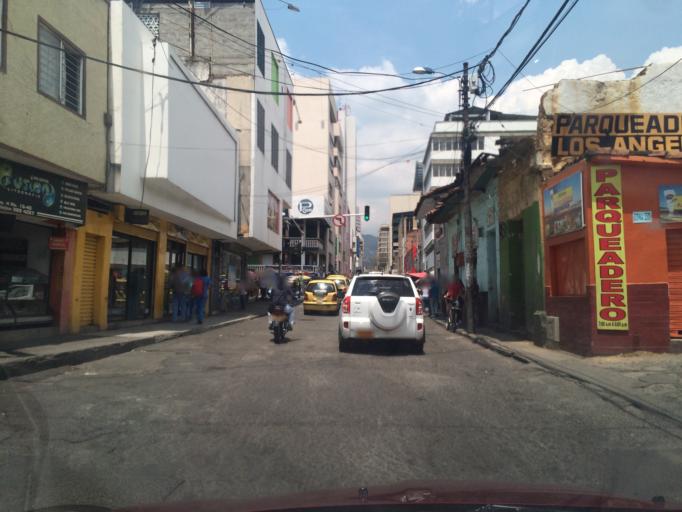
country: CO
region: Valle del Cauca
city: Cali
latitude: 3.4539
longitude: -76.5294
